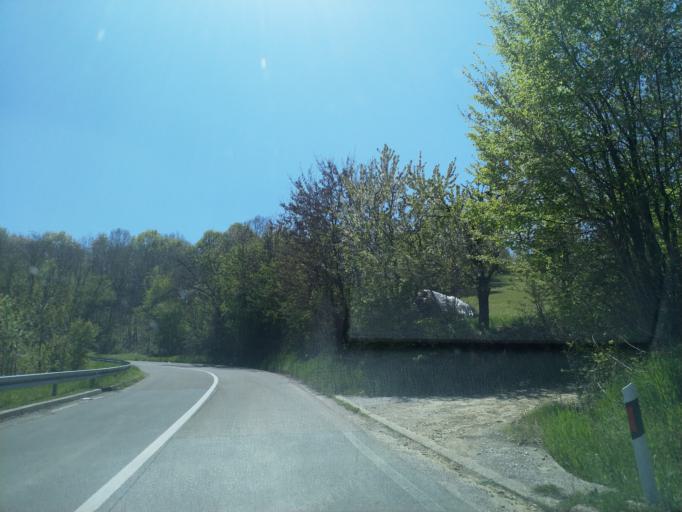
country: RS
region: Central Serbia
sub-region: Belgrade
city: Lazarevac
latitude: 44.3666
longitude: 20.3388
